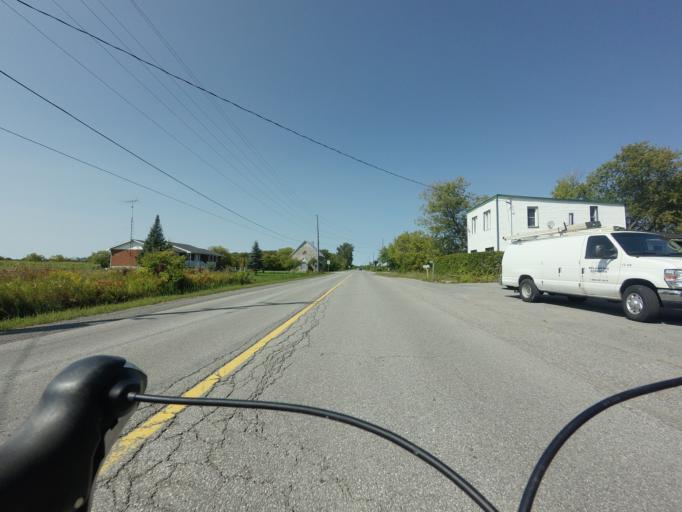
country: CA
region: Ontario
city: Arnprior
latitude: 45.4743
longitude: -76.1147
